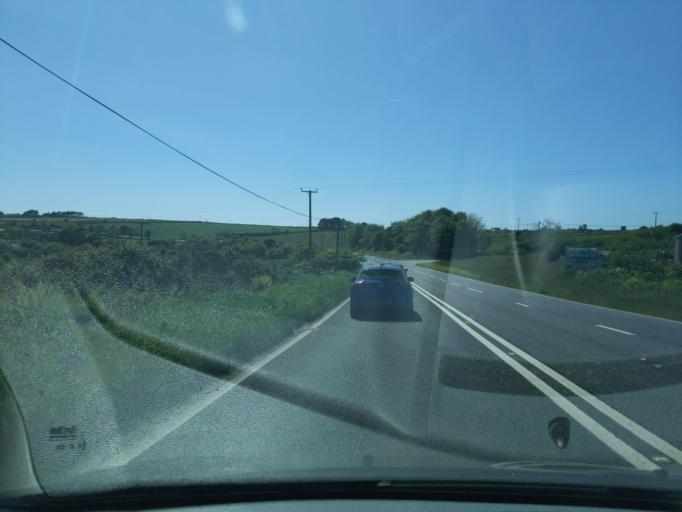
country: GB
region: England
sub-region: Cornwall
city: Wendron
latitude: 50.1499
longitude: -5.2053
